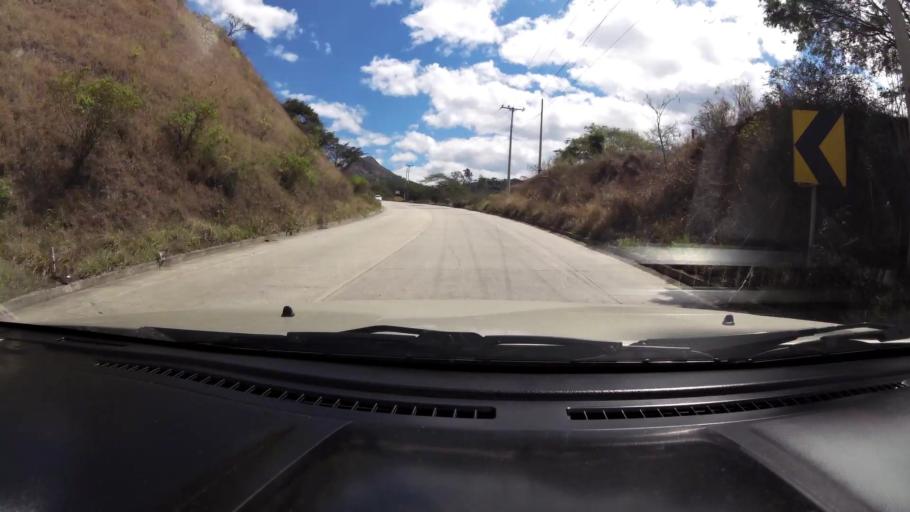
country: EC
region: Azuay
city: Cuenca
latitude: -3.2244
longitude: -79.2057
